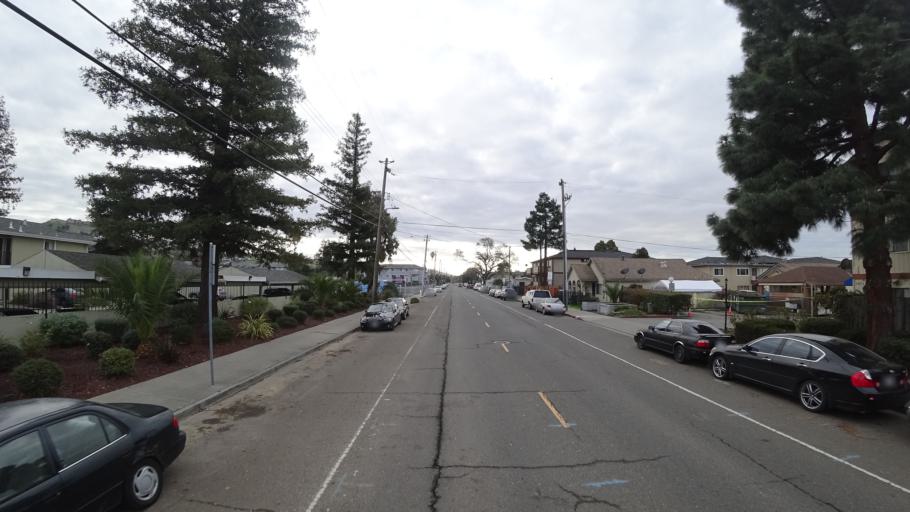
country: US
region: California
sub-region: Alameda County
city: Hayward
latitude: 37.6307
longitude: -122.0521
